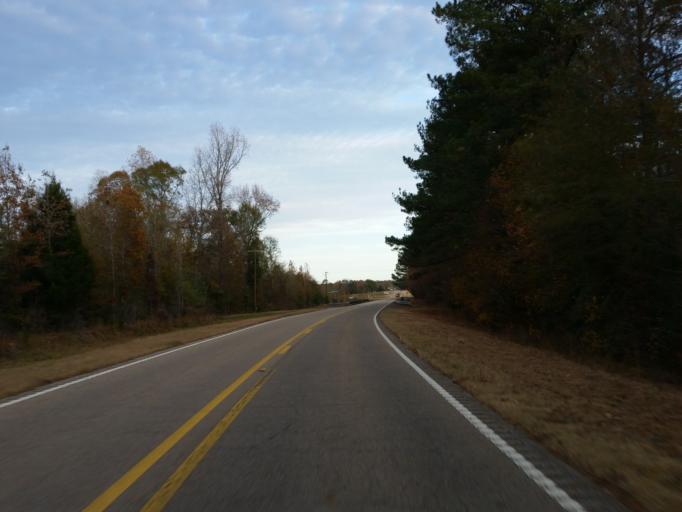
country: US
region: Alabama
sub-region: Sumter County
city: York
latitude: 32.4267
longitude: -88.4602
